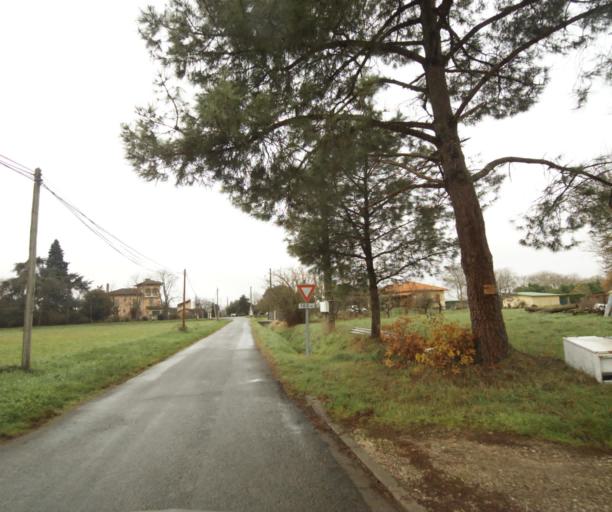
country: FR
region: Midi-Pyrenees
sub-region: Departement de la Haute-Garonne
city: Villemur-sur-Tarn
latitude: 43.8706
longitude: 1.4678
